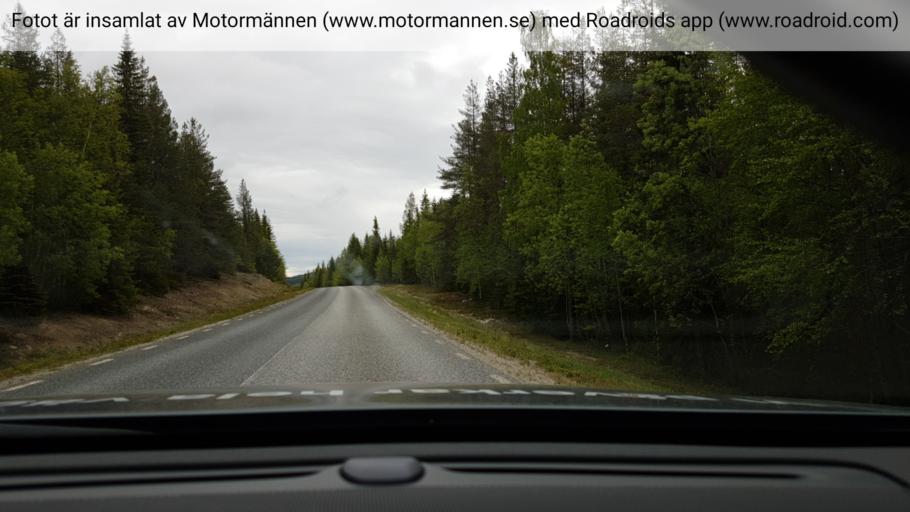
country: SE
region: Vaesterbotten
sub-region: Asele Kommun
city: Insjon
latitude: 64.3488
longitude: 17.8525
